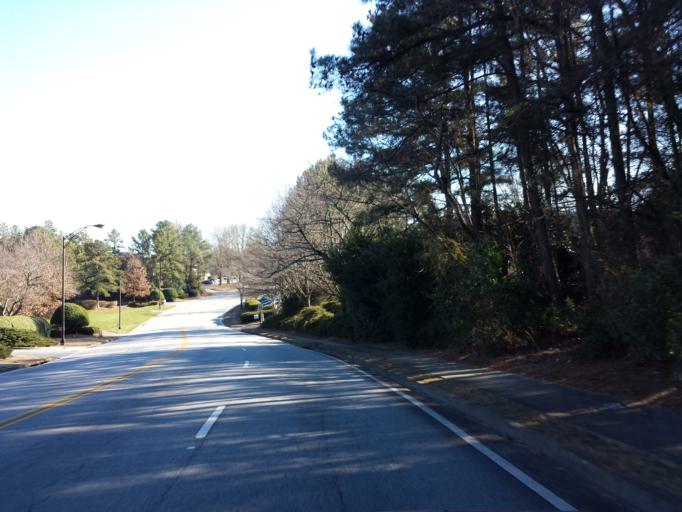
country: US
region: Georgia
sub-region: Cobb County
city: Smyrna
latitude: 33.9084
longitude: -84.4793
